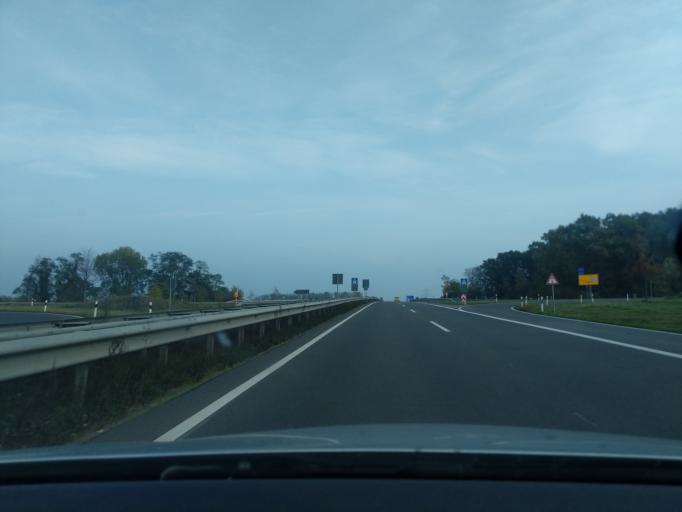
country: DE
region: Lower Saxony
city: Stade
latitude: 53.5815
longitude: 9.5026
